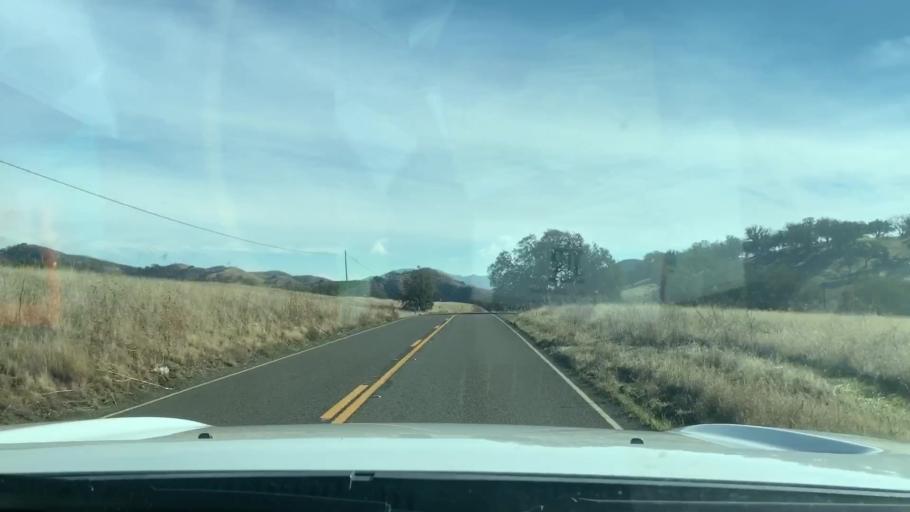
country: US
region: California
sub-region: Fresno County
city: Coalinga
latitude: 36.0972
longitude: -120.5281
